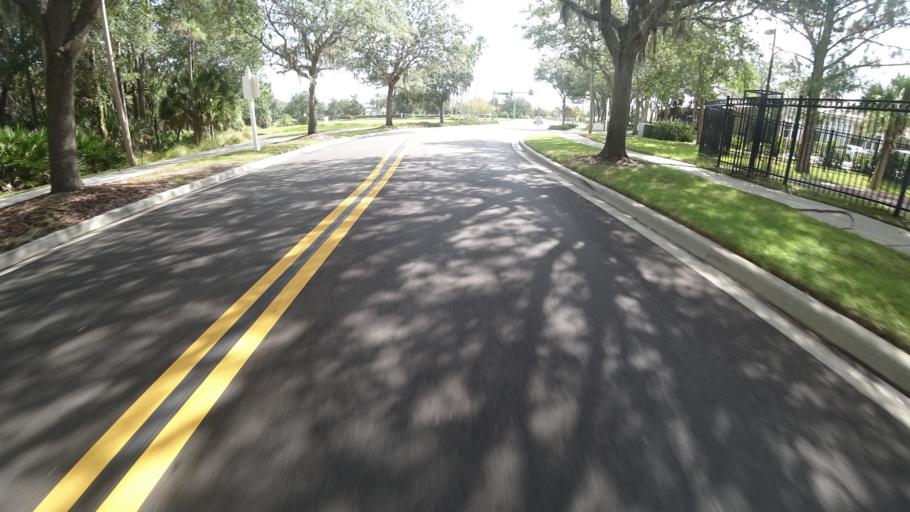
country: US
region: Florida
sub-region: Sarasota County
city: The Meadows
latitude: 27.3937
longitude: -82.4387
